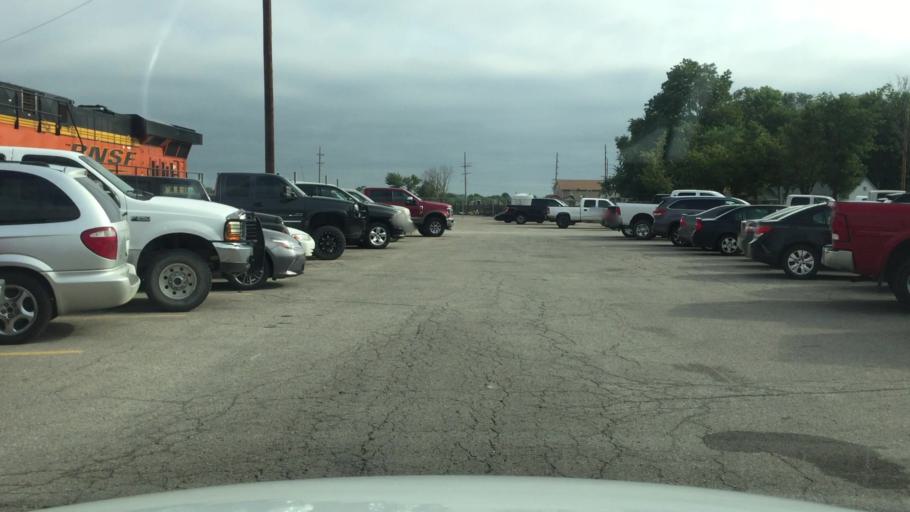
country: US
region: Kansas
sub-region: Shawnee County
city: Topeka
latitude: 39.0598
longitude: -95.6562
